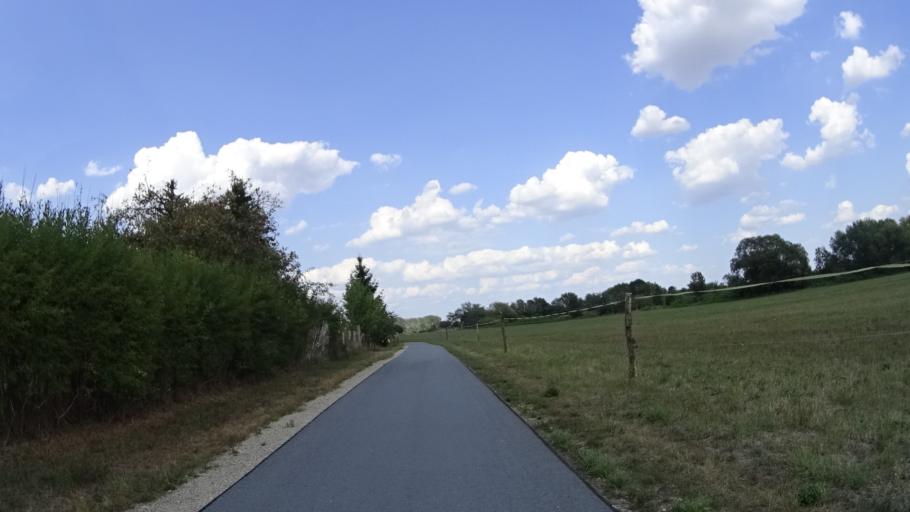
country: DE
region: Saxony
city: Ostritz
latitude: 51.0446
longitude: 14.9509
